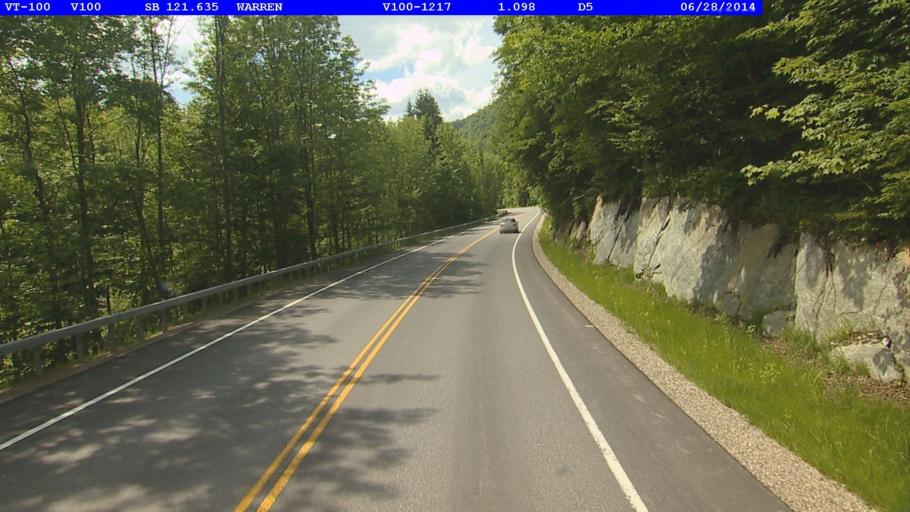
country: US
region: Vermont
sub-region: Washington County
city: Northfield
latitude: 44.0752
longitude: -72.8599
